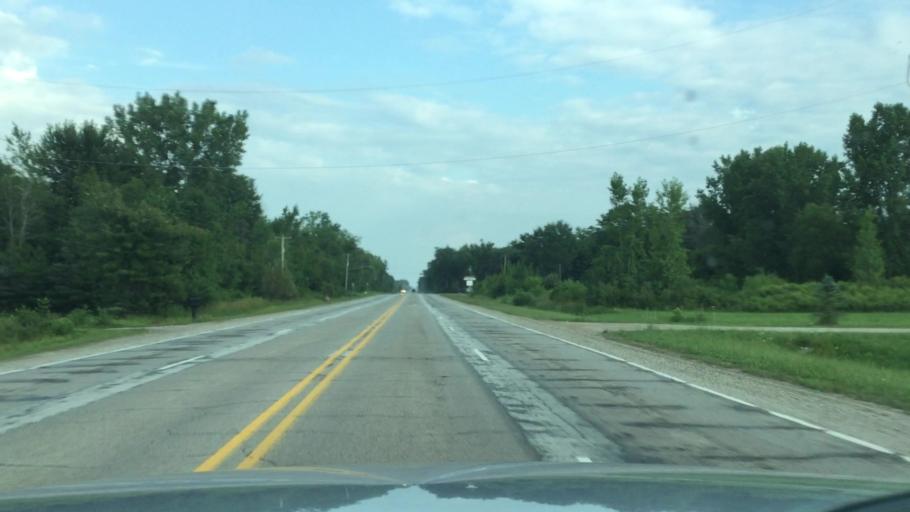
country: US
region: Michigan
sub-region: Saginaw County
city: Birch Run
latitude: 43.2810
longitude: -83.7927
